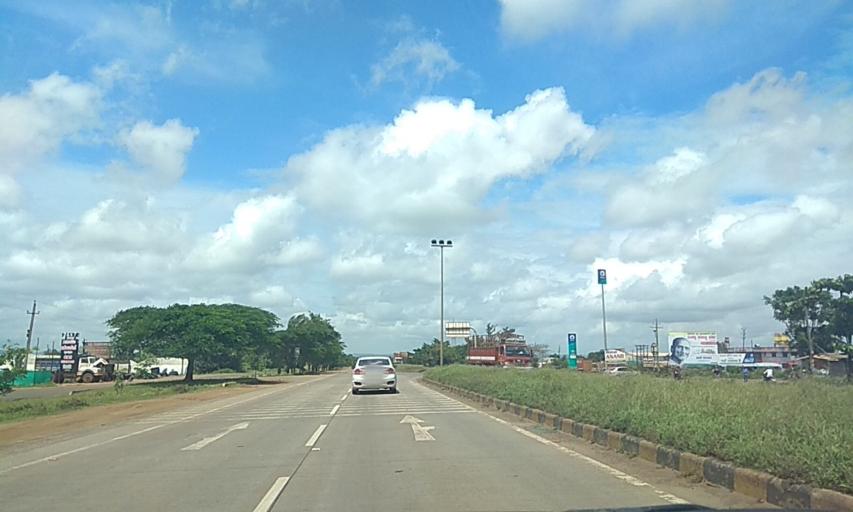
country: IN
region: Karnataka
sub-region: Belgaum
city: Sankeshwar
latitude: 16.1472
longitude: 74.5172
